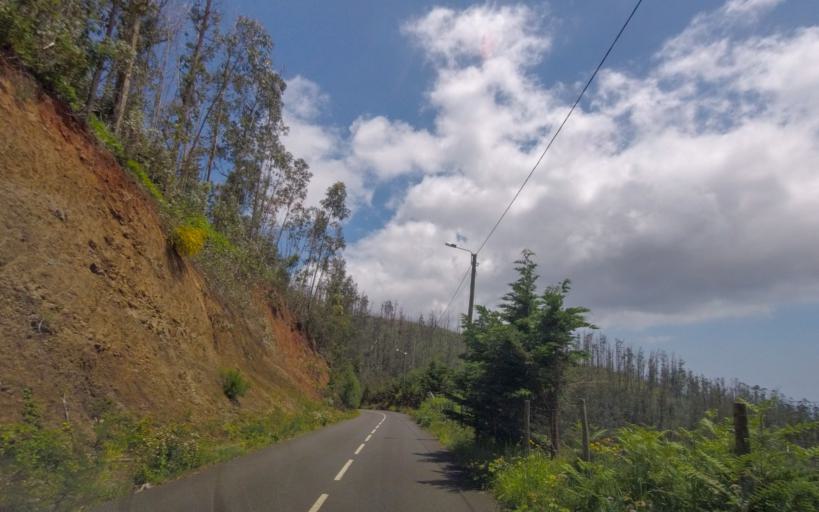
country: PT
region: Madeira
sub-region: Funchal
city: Nossa Senhora do Monte
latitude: 32.6803
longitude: -16.8835
